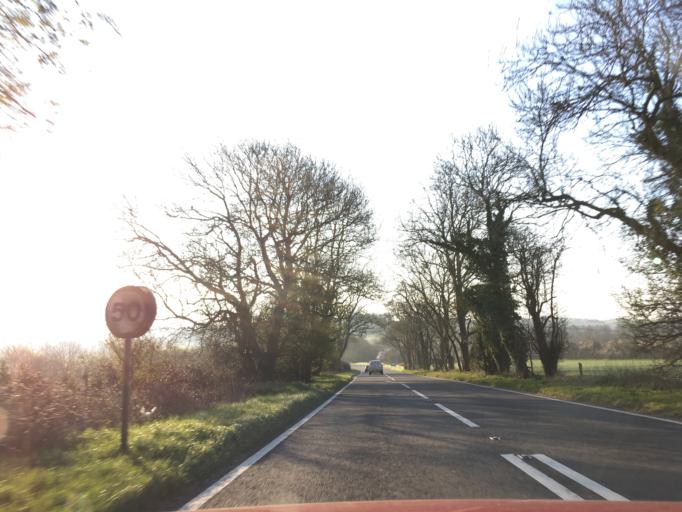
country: GB
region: England
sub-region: Gloucestershire
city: Shipton Village
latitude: 51.8651
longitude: -1.9682
